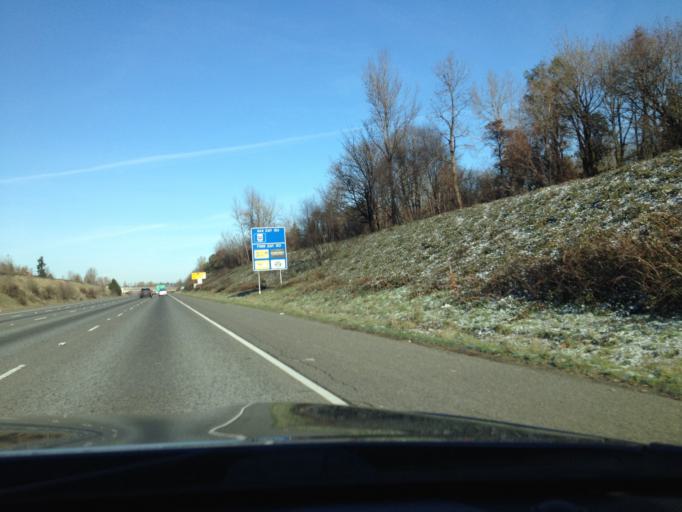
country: US
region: Washington
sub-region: King County
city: SeaTac
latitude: 47.4382
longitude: -122.2688
